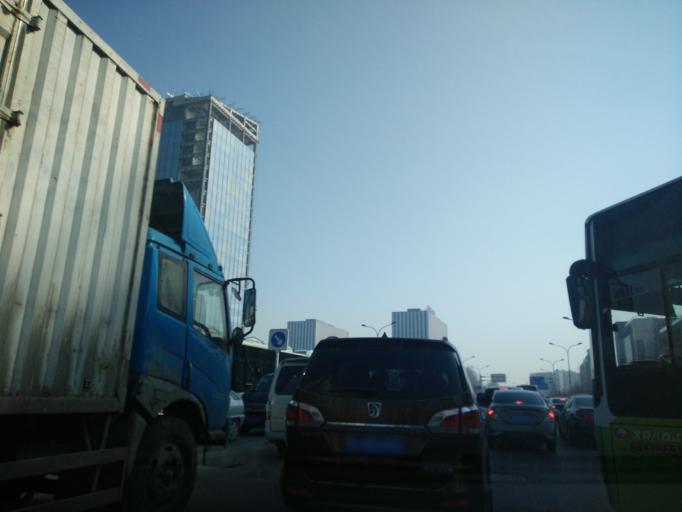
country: CN
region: Beijing
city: Laiguangying
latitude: 40.0192
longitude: 116.4612
